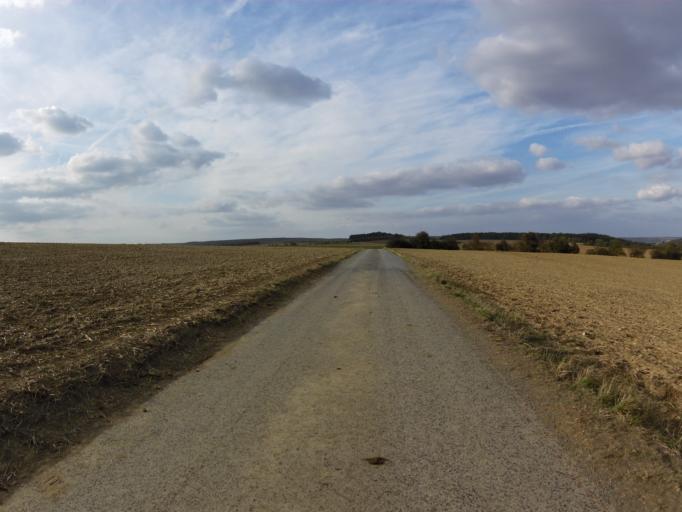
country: DE
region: Bavaria
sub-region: Regierungsbezirk Unterfranken
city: Reichenberg
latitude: 49.7227
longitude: 9.9485
